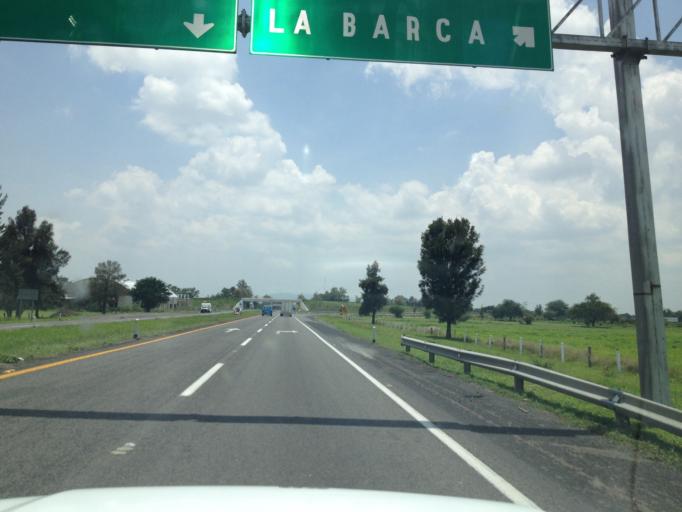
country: MX
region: Jalisco
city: La Barca
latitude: 20.3221
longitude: -102.5323
